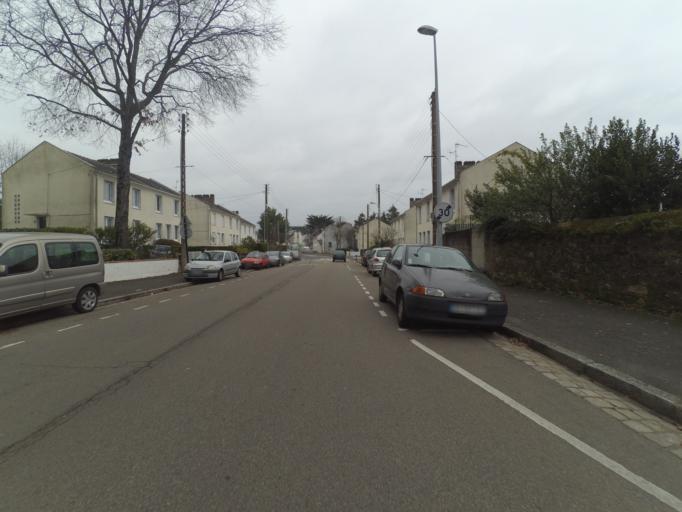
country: FR
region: Pays de la Loire
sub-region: Departement de la Loire-Atlantique
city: Nantes
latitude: 47.2192
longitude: -1.5969
